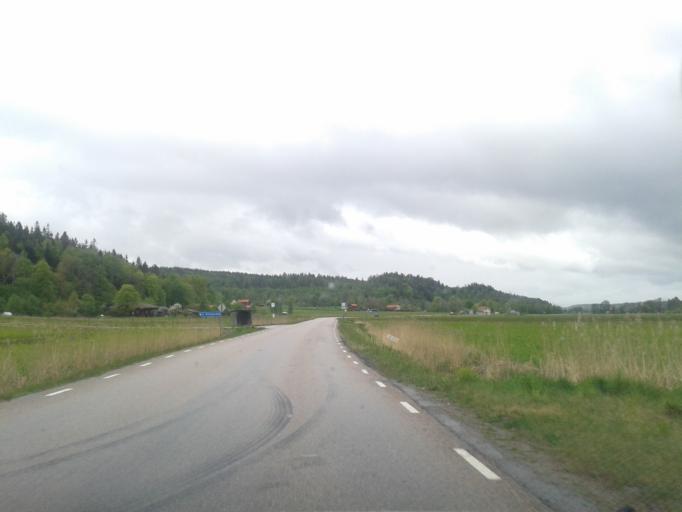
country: SE
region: Vaestra Goetaland
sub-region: Ale Kommun
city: Alvangen
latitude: 57.9948
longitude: 12.1199
